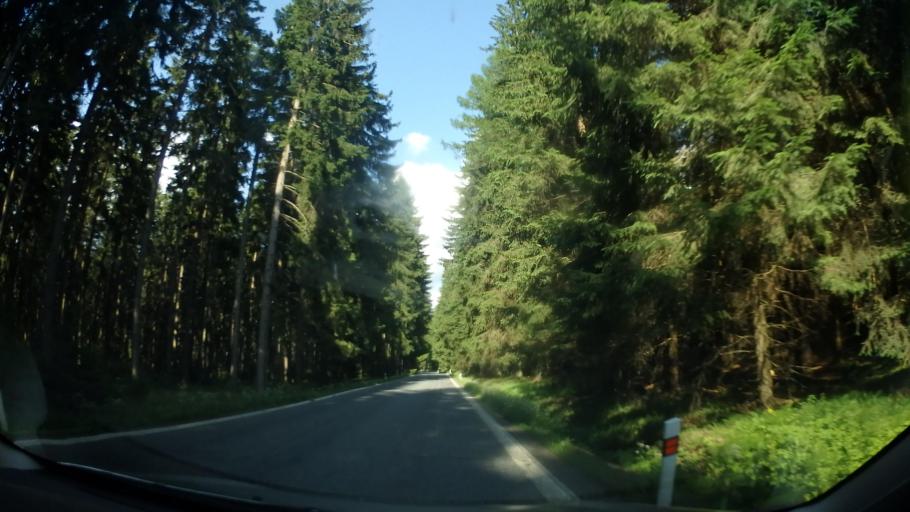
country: CZ
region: Vysocina
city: Heralec
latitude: 49.6691
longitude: 15.9810
